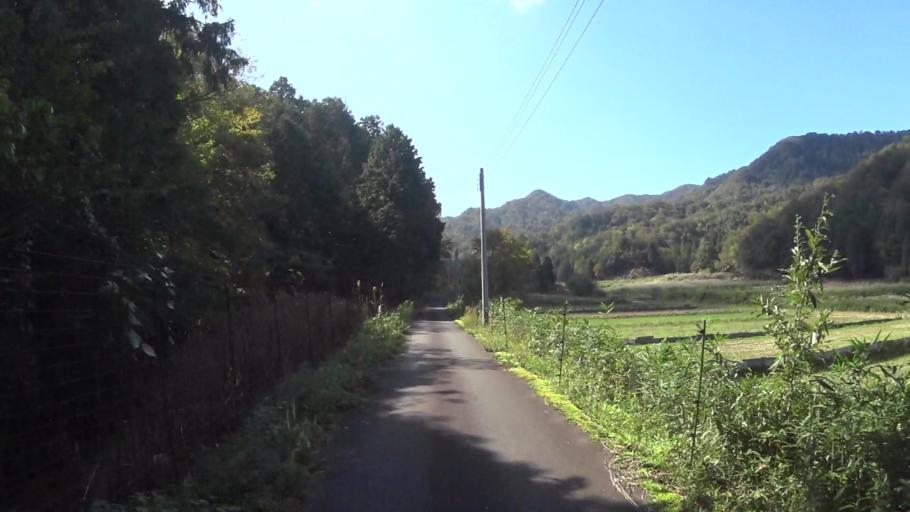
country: JP
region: Hyogo
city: Toyooka
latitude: 35.5633
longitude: 134.9196
